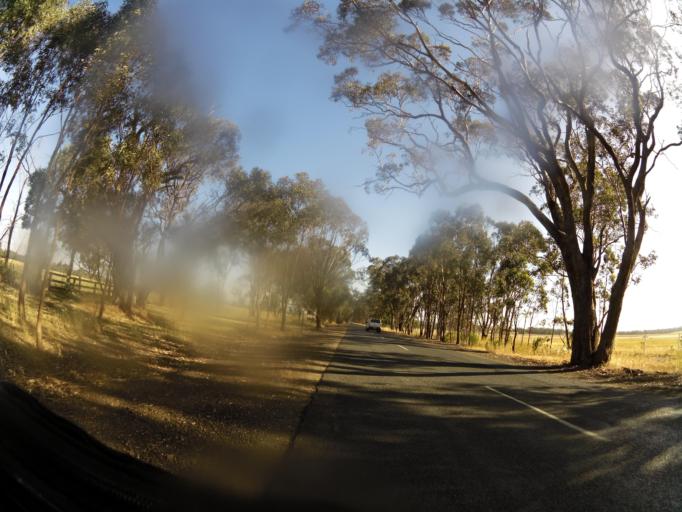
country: AU
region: Victoria
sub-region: Murrindindi
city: Kinglake West
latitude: -36.9763
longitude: 145.1101
